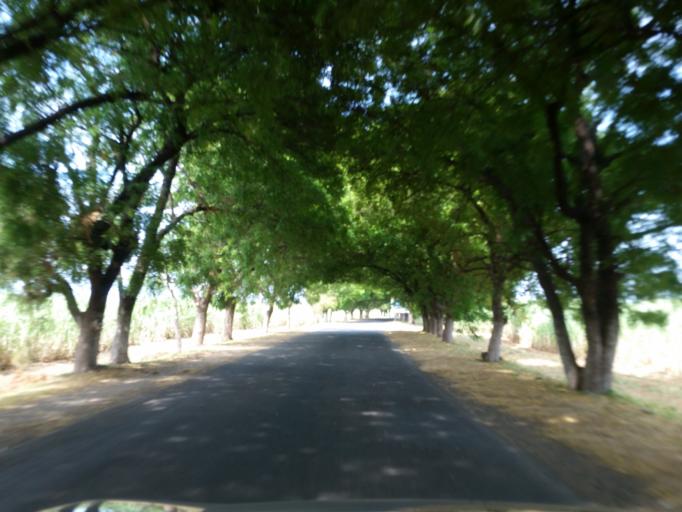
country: NI
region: Managua
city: Masachapa
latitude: 11.7900
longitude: -86.5065
